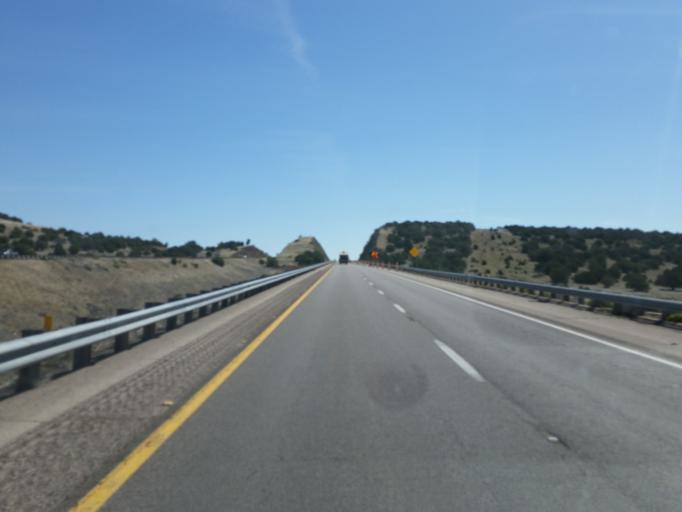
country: US
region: Arizona
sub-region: Mohave County
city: Peach Springs
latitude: 35.2369
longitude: -113.2063
